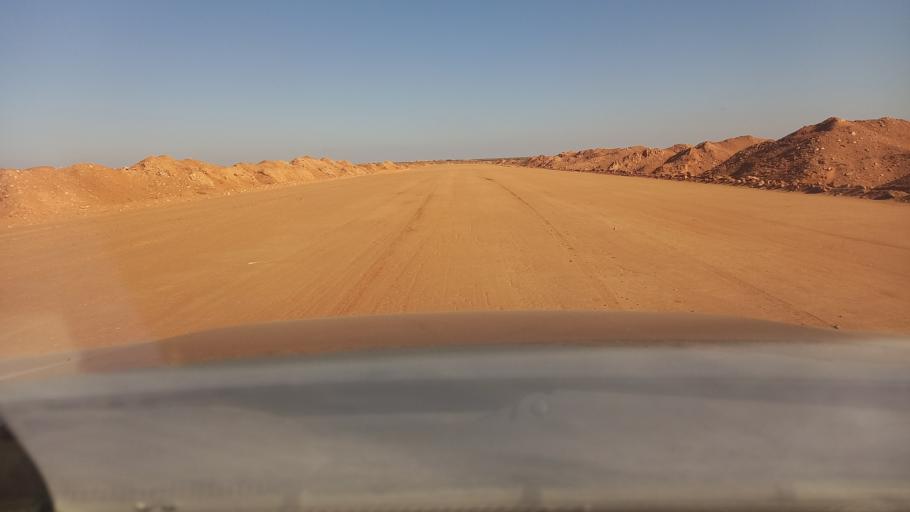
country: TN
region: Madanin
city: Medenine
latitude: 33.1646
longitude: 10.5216
